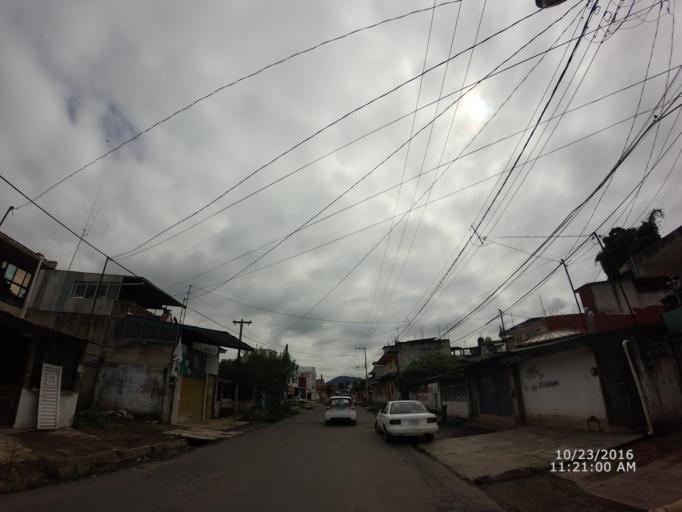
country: MX
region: Veracruz
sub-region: Tlalnelhuayocan
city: Guadalupe Victoria
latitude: 19.5512
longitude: -96.9515
